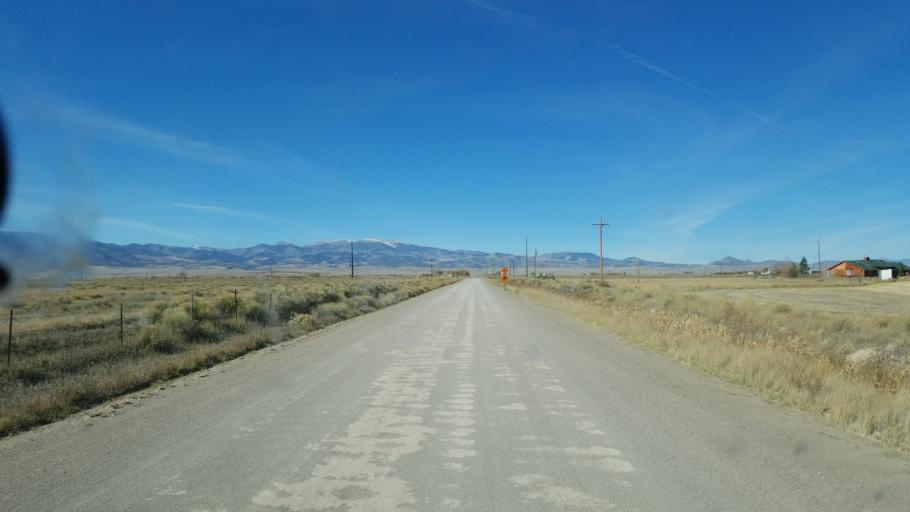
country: US
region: Colorado
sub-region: Rio Grande County
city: Monte Vista
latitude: 37.5313
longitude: -106.0901
